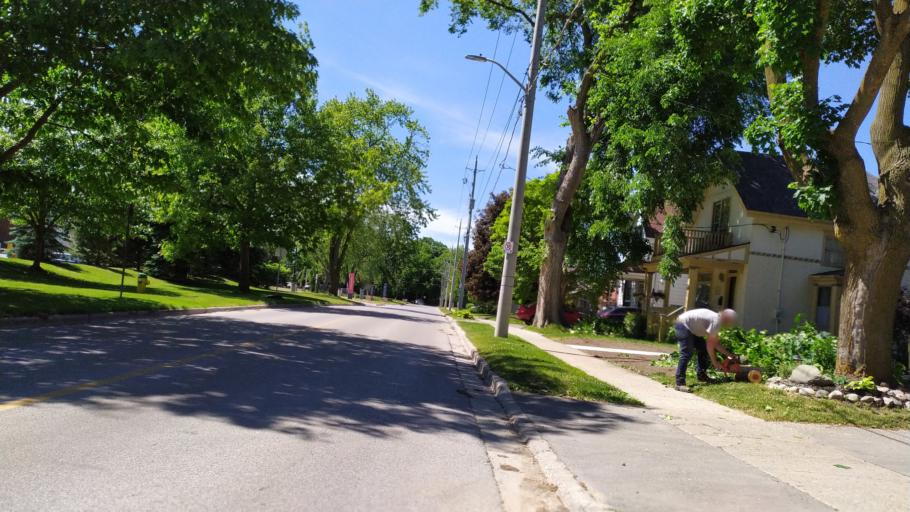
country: CA
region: Ontario
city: Stratford
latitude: 43.3684
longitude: -80.9937
